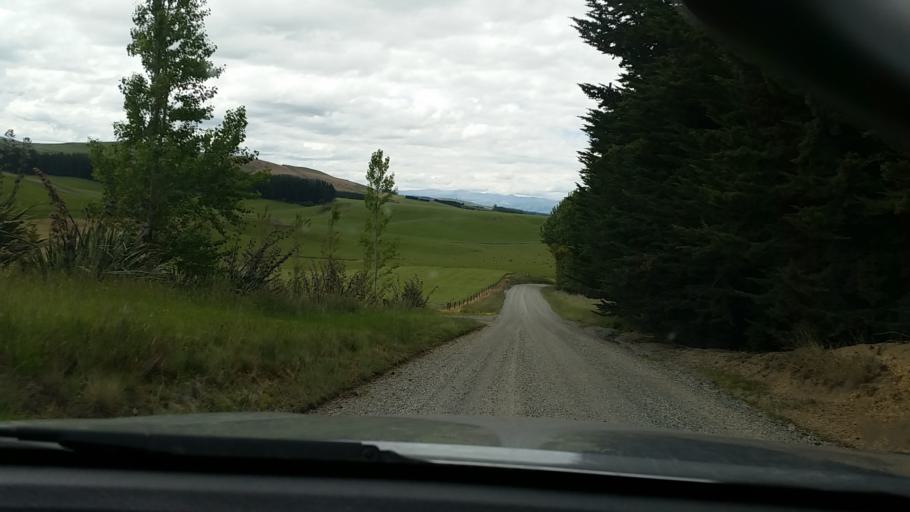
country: NZ
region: Otago
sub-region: Queenstown-Lakes District
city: Kingston
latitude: -45.7724
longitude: 168.5944
